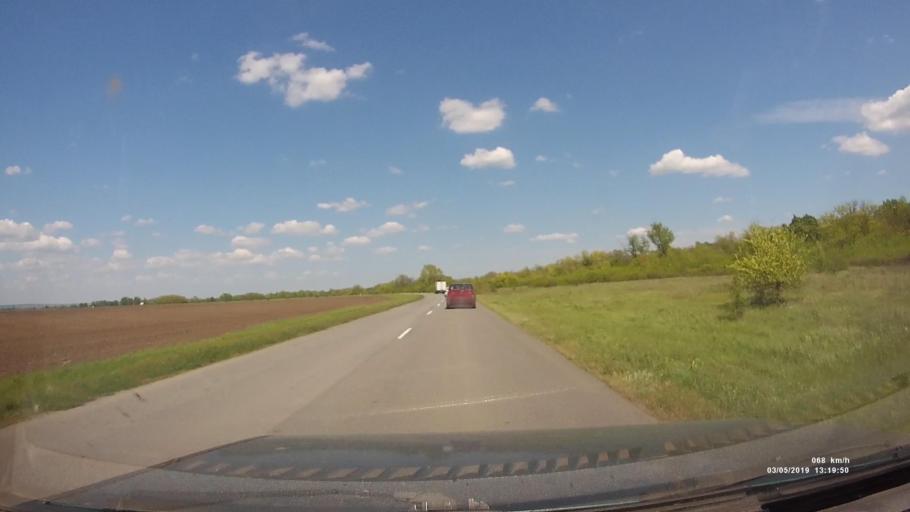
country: RU
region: Rostov
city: Semikarakorsk
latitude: 47.5402
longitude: 40.7515
